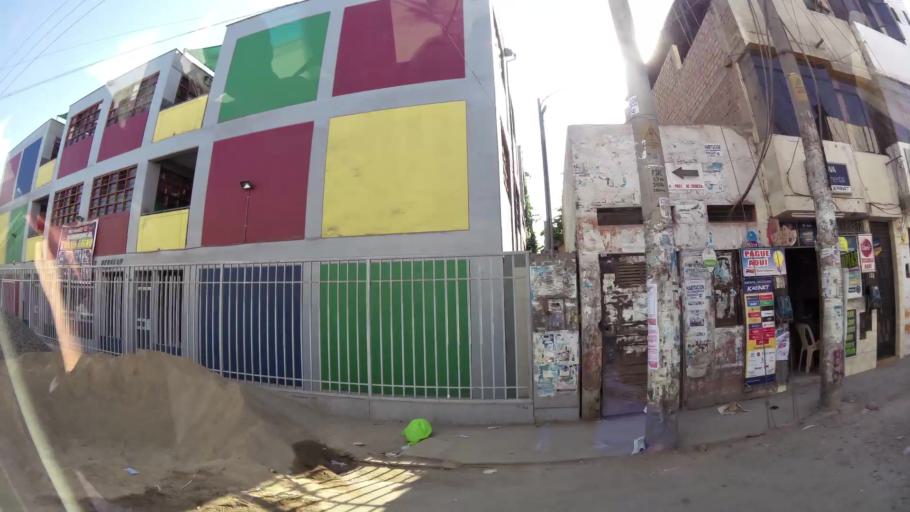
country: PE
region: Ica
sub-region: Provincia de Chincha
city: Chincha Alta
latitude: -13.4184
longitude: -76.1360
